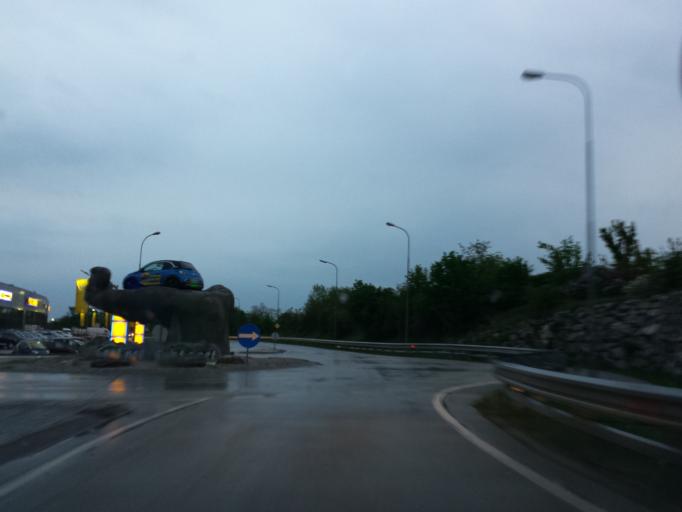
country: AT
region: Lower Austria
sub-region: Politischer Bezirk Modling
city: Brunn am Gebirge
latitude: 48.1066
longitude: 16.3061
